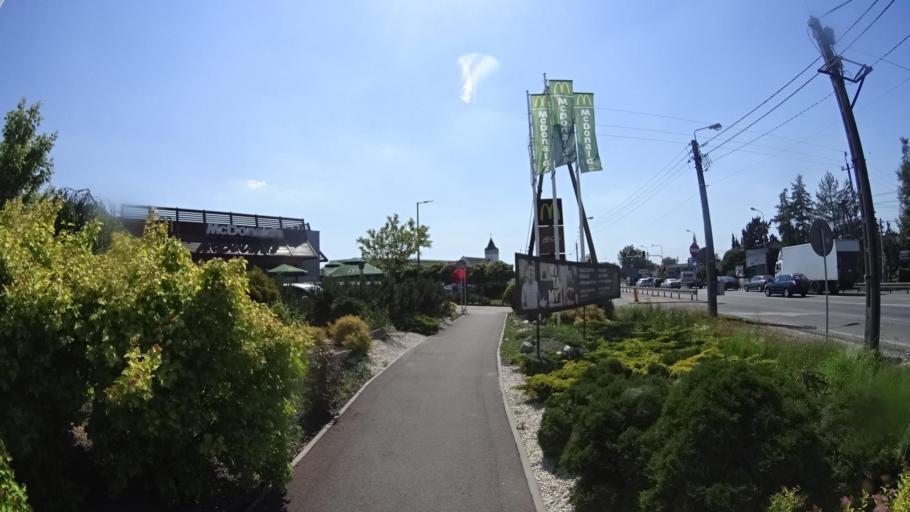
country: PL
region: Masovian Voivodeship
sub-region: Powiat warszawski zachodni
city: Blonie
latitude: 52.1999
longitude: 20.6244
